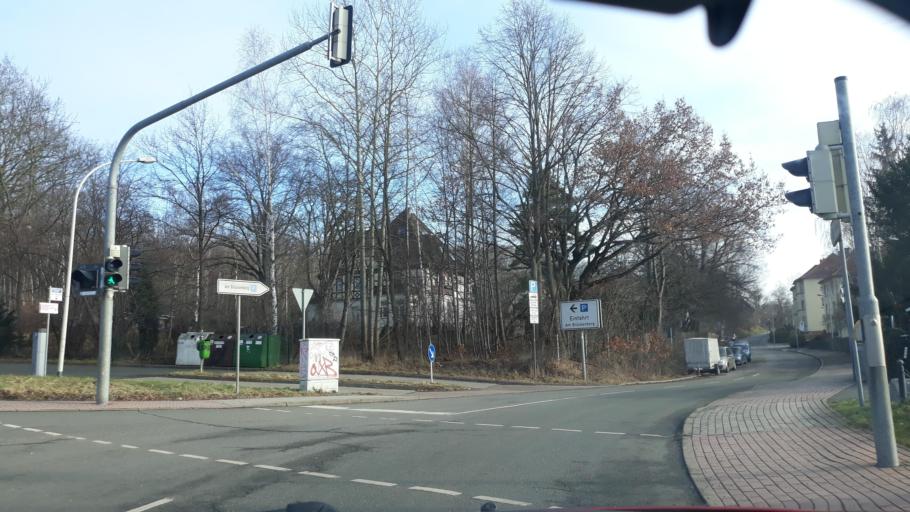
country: DE
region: Saxony
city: Zwickau
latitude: 50.7155
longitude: 12.5040
